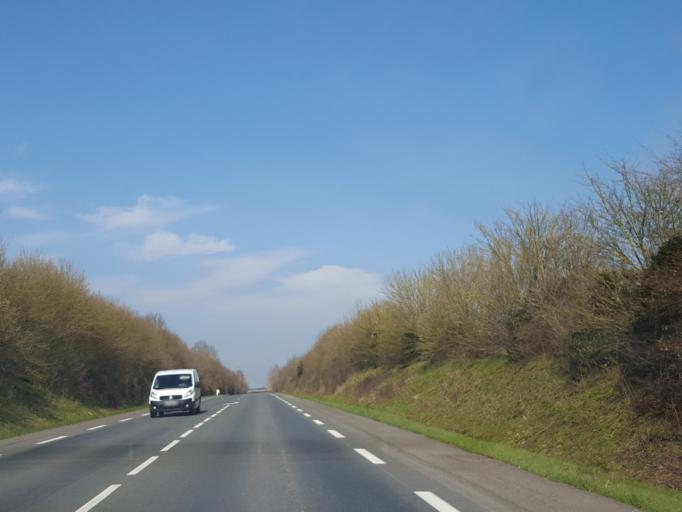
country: FR
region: Pays de la Loire
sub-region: Departement de la Vendee
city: Saint-Fulgent
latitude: 46.8400
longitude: -1.1621
